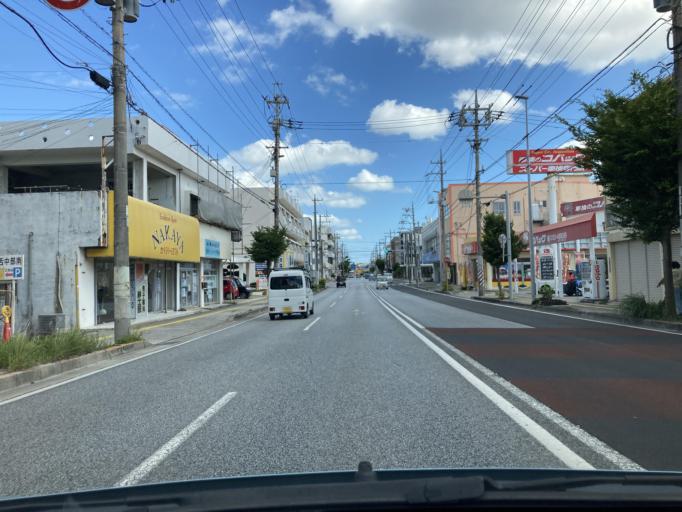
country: JP
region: Okinawa
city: Okinawa
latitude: 26.3379
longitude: 127.8092
